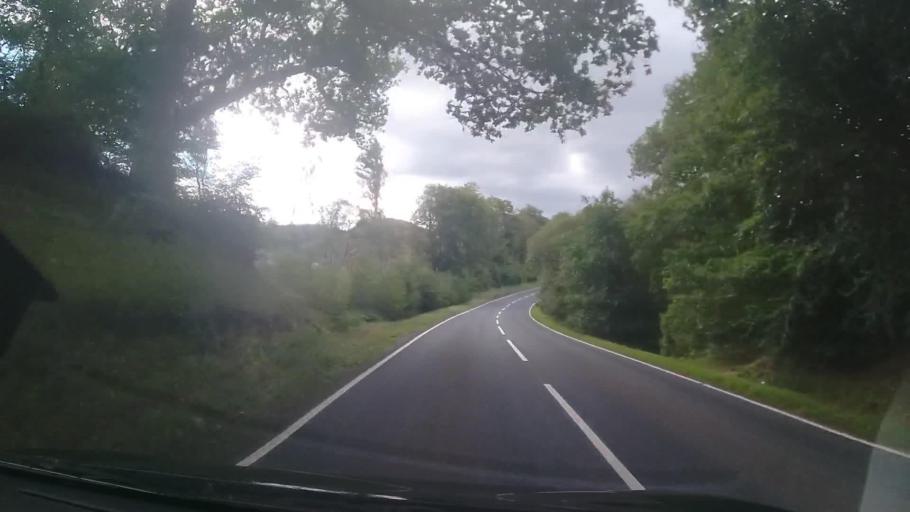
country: GB
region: Scotland
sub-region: Argyll and Bute
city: Garelochhead
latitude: 56.4018
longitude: -5.0188
